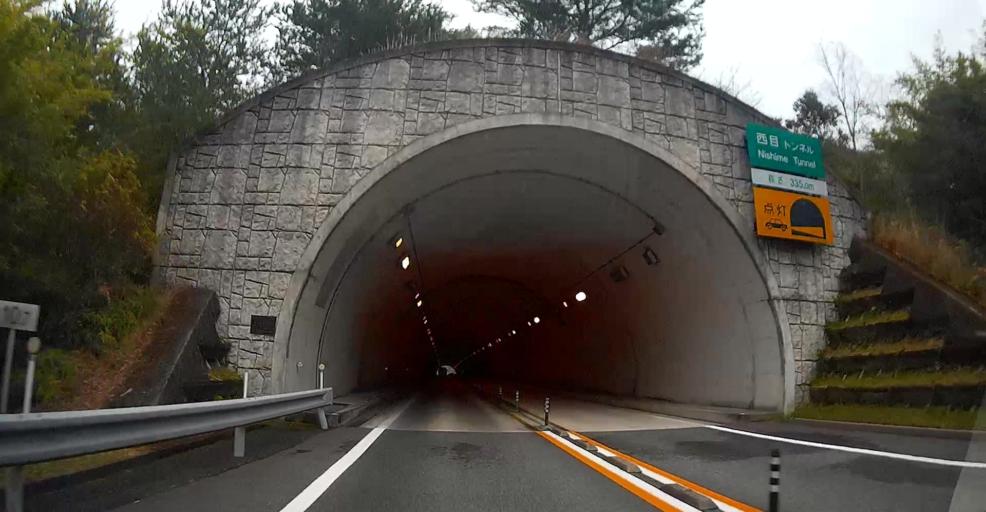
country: JP
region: Kumamoto
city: Yatsushiro
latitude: 32.5084
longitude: 130.4058
